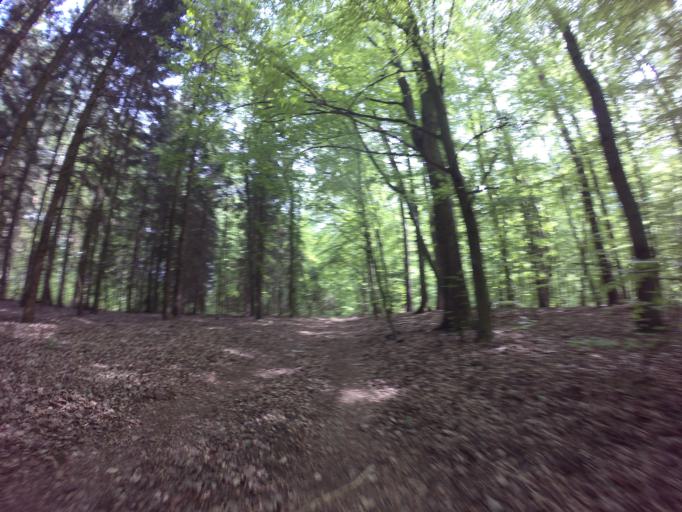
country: PL
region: West Pomeranian Voivodeship
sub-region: Powiat choszczenski
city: Choszczno
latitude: 53.2286
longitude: 15.4093
